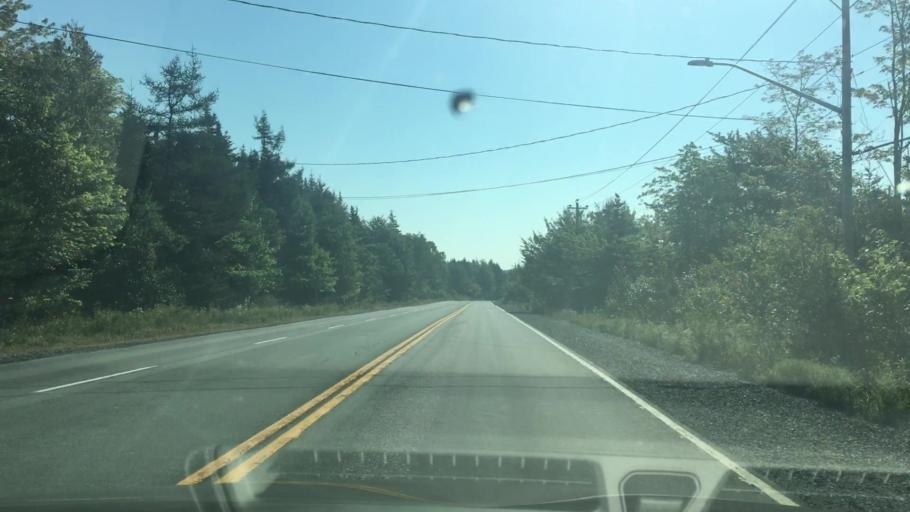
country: CA
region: Nova Scotia
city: Cole Harbour
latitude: 44.7785
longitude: -63.0770
